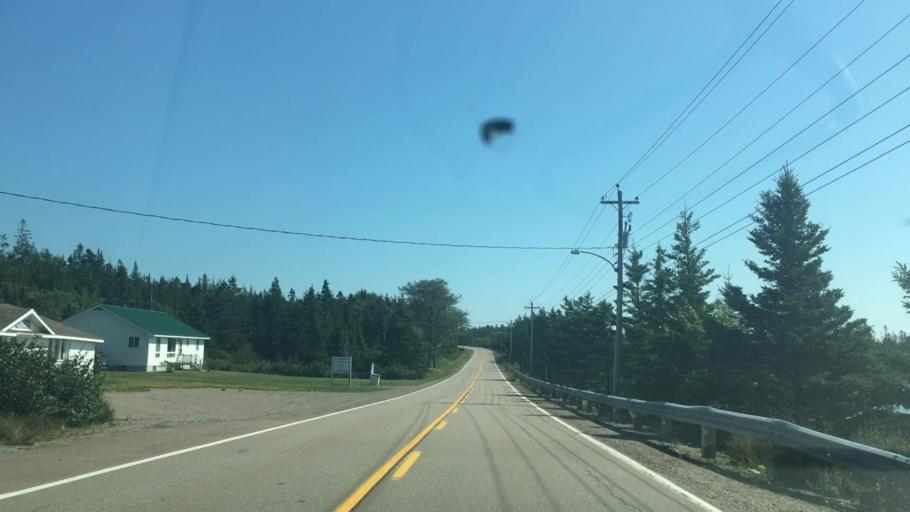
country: CA
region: Nova Scotia
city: Antigonish
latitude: 45.0221
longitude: -62.0125
